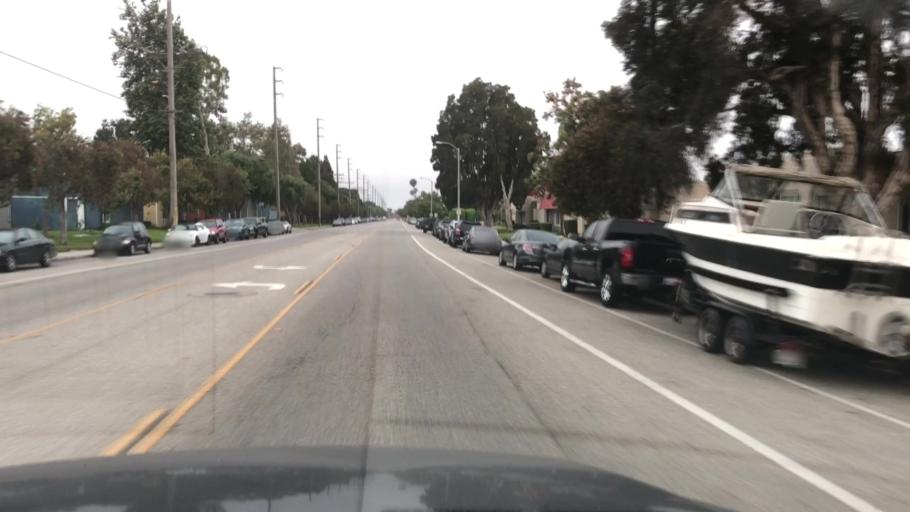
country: US
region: California
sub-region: Ventura County
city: Channel Islands Beach
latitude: 34.1813
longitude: -119.2097
